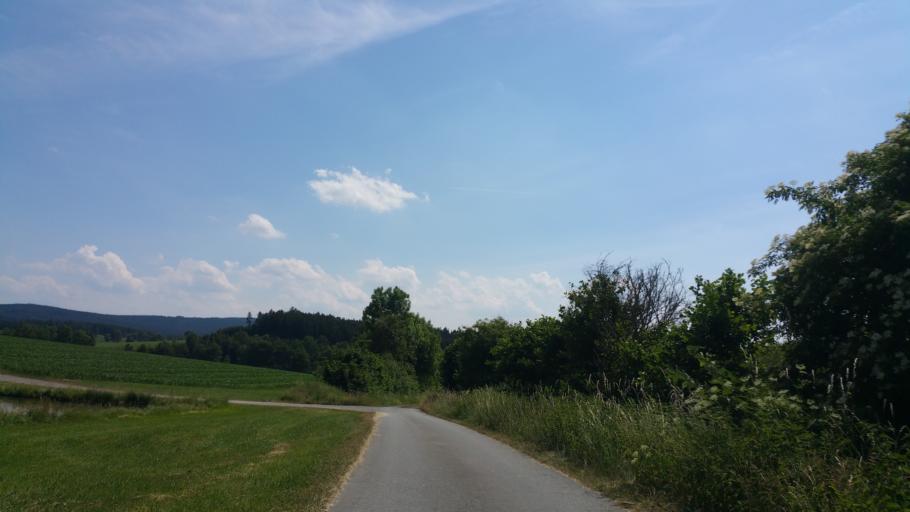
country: DE
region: Bavaria
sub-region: Upper Franconia
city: Weissdorf
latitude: 50.2034
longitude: 11.8923
